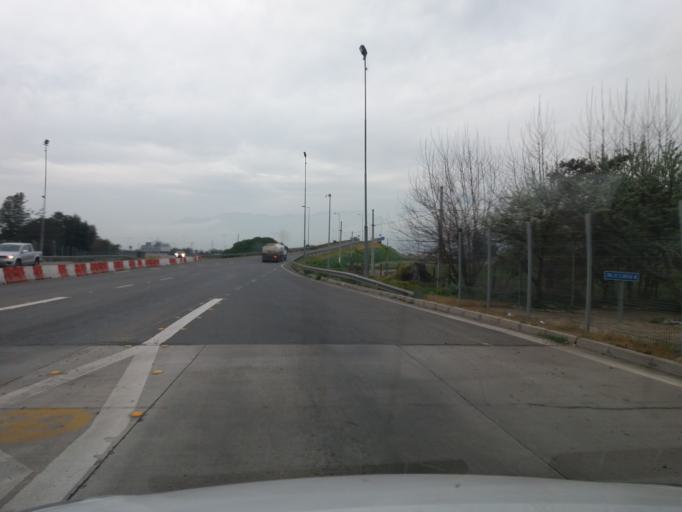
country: CL
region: Valparaiso
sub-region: Provincia de Quillota
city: Quillota
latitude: -32.9275
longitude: -71.2863
